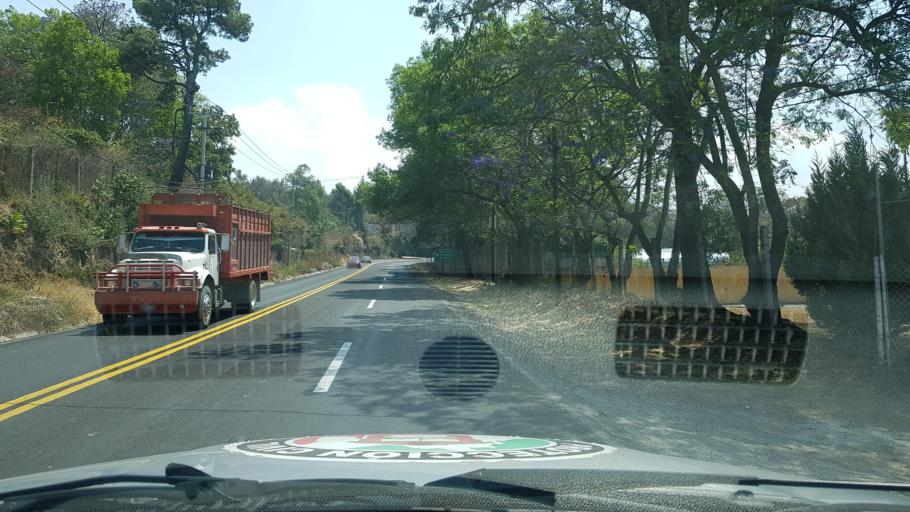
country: MX
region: Mexico
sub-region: Tepetlixpa
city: Nepantla de Sor Juana Ines de la Cruz
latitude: 18.9892
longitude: -98.8322
